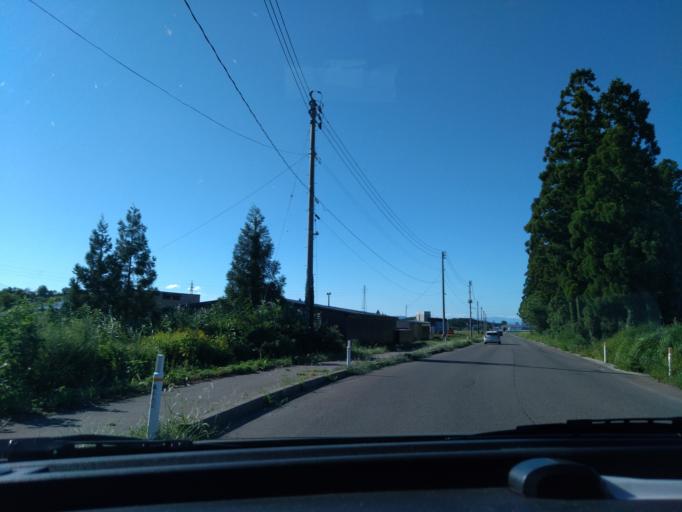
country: JP
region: Akita
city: Yokotemachi
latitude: 39.2840
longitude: 140.5564
